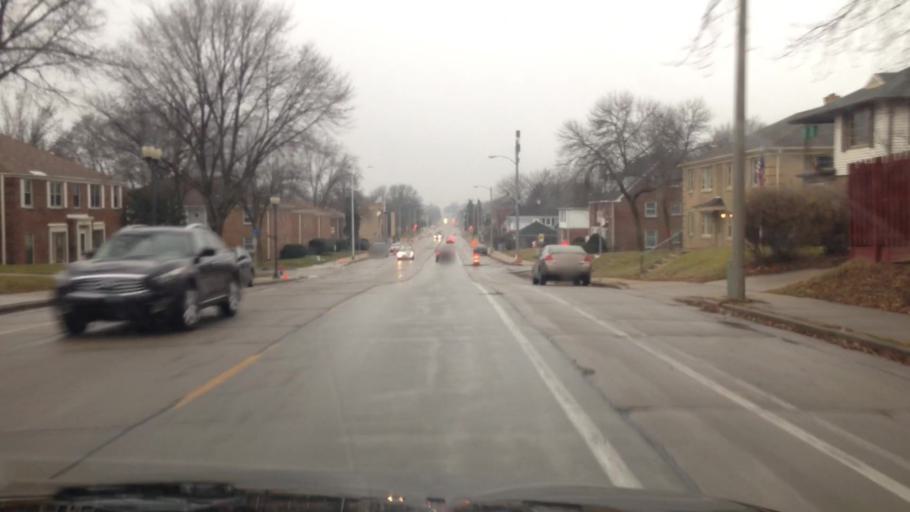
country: US
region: Wisconsin
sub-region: Milwaukee County
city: Wauwatosa
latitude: 43.0681
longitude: -87.9939
